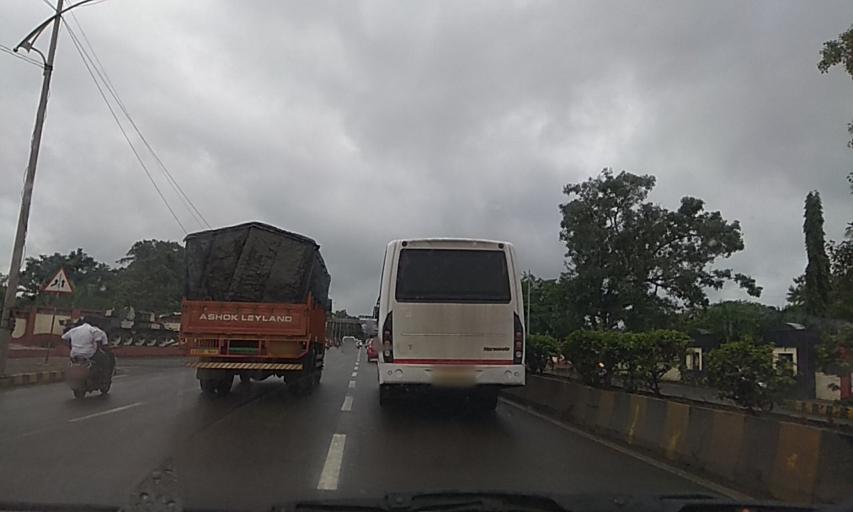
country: IN
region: Maharashtra
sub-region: Pune Division
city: Khadki
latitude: 18.5517
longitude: 73.8665
